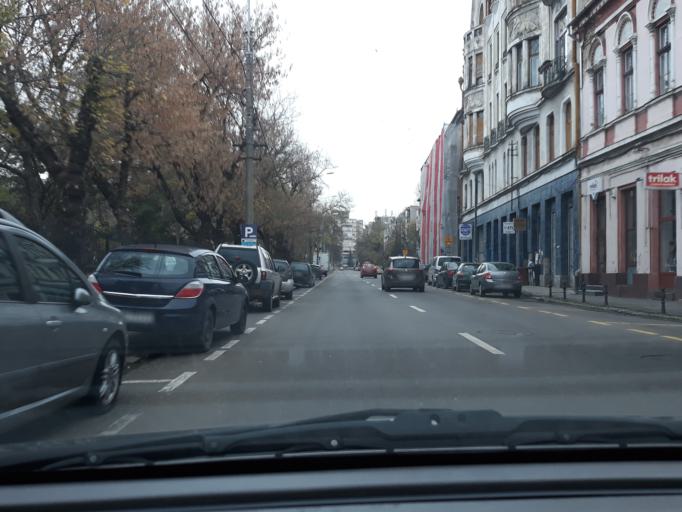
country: RO
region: Bihor
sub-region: Comuna Biharea
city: Oradea
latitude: 47.0527
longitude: 21.9330
